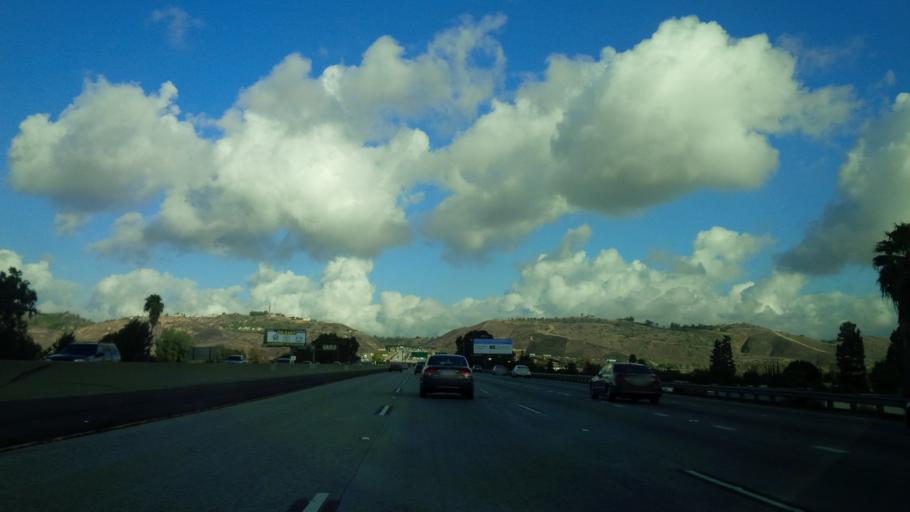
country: US
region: California
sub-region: Los Angeles County
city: Diamond Bar
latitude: 34.0538
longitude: -117.8029
